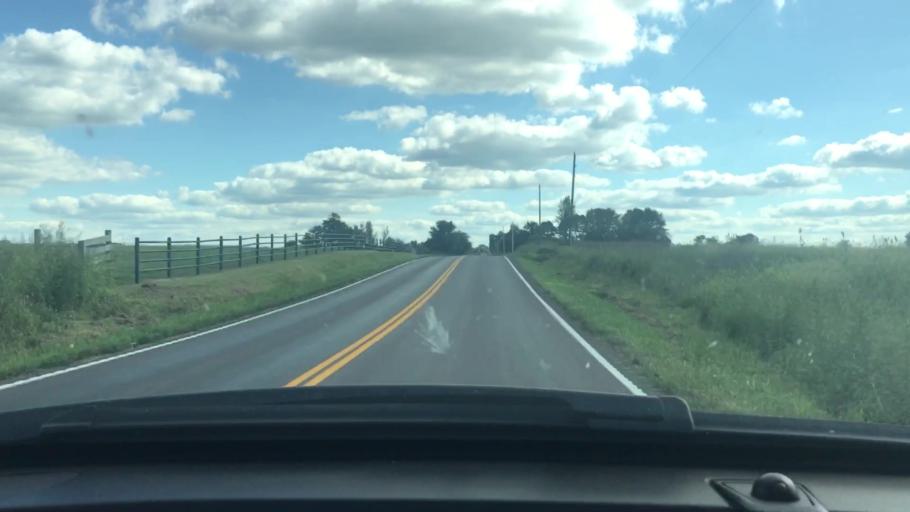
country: US
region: Missouri
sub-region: Wright County
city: Mountain Grove
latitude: 37.1742
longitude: -92.2670
